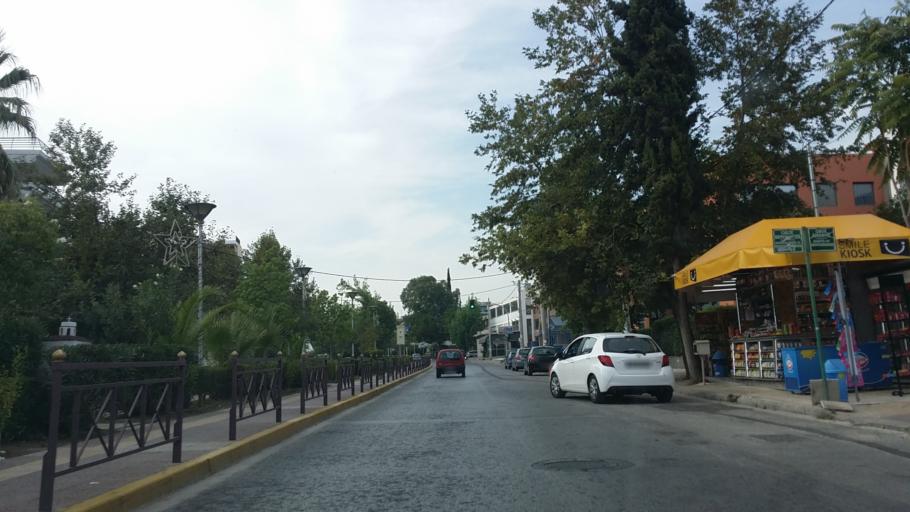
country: GR
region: Attica
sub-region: Nomarchia Athinas
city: Irakleio
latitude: 38.0420
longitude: 23.7749
